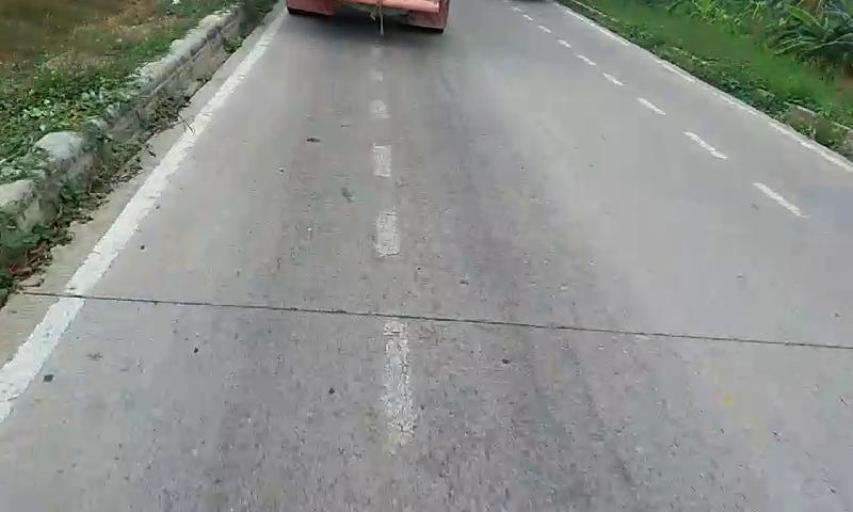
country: ID
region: West Java
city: Bekasi
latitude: -6.1489
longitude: 106.9703
